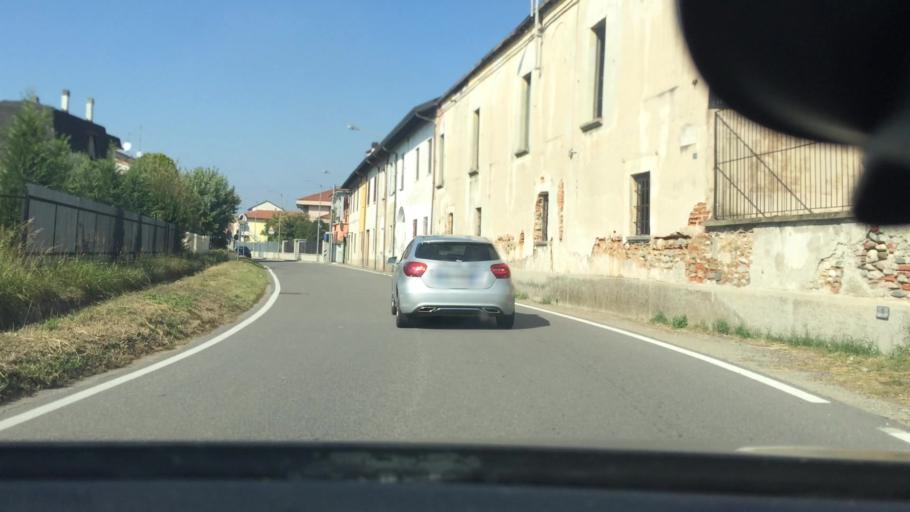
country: IT
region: Lombardy
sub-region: Citta metropolitana di Milano
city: Casate
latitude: 45.4915
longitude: 8.8298
